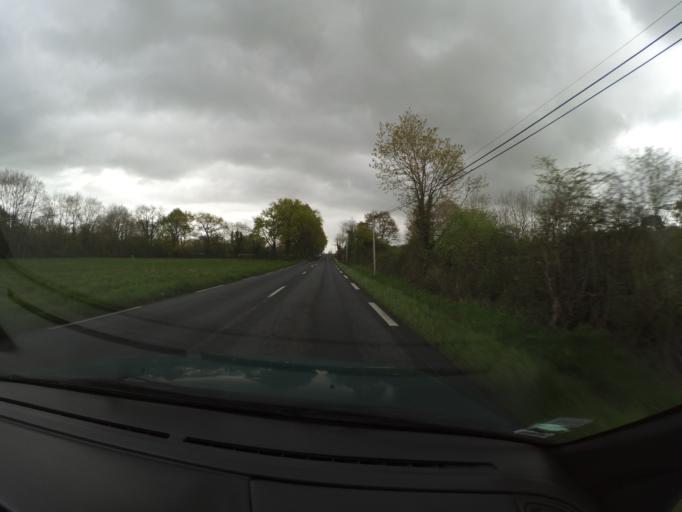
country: FR
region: Pays de la Loire
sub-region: Departement de la Loire-Atlantique
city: La Remaudiere
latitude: 47.1998
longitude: -1.2467
